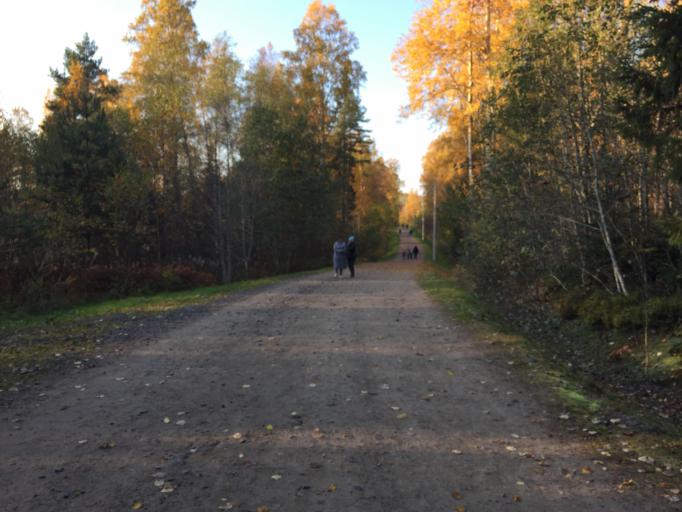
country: RU
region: Leningrad
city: Priozersk
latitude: 61.2831
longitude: 30.0932
